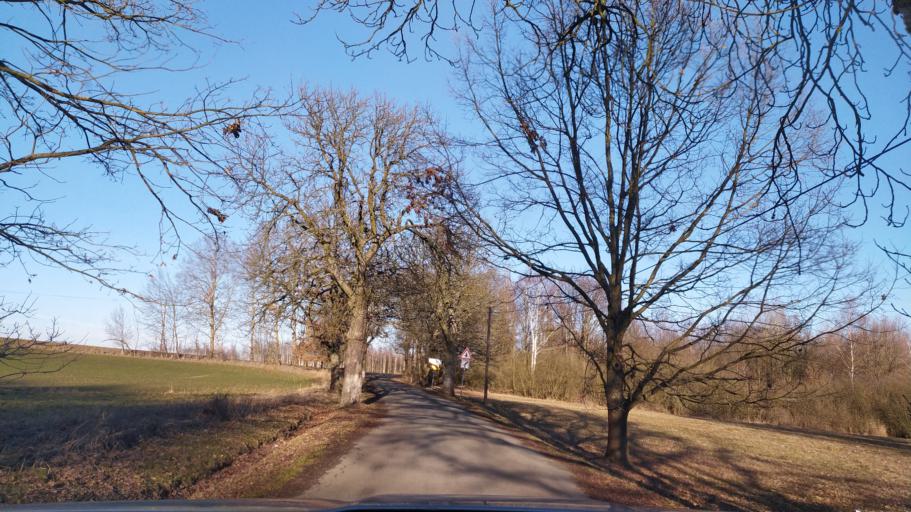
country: CZ
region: Karlovarsky
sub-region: Okres Cheb
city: Frantiskovy Lazne
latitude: 50.1140
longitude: 12.3179
